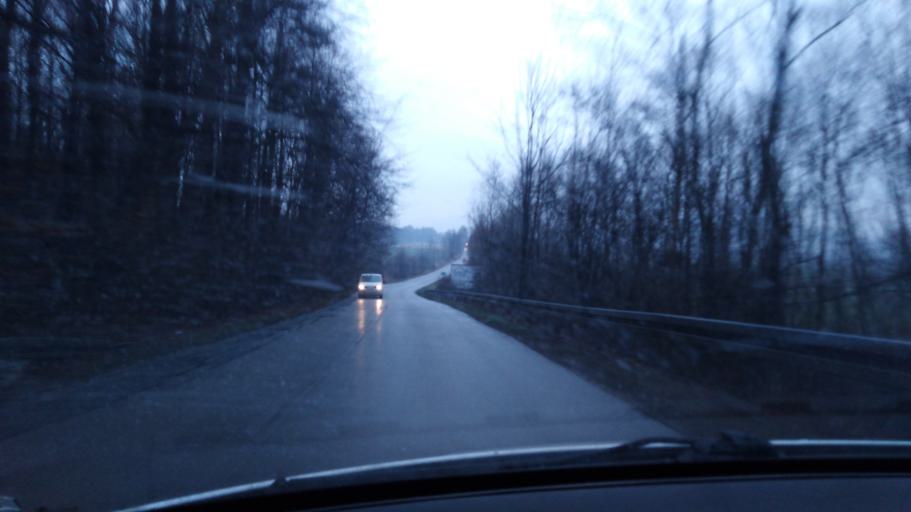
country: PL
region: Silesian Voivodeship
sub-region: Powiat zywiecki
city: Radziechowy
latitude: 49.6344
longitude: 19.1542
